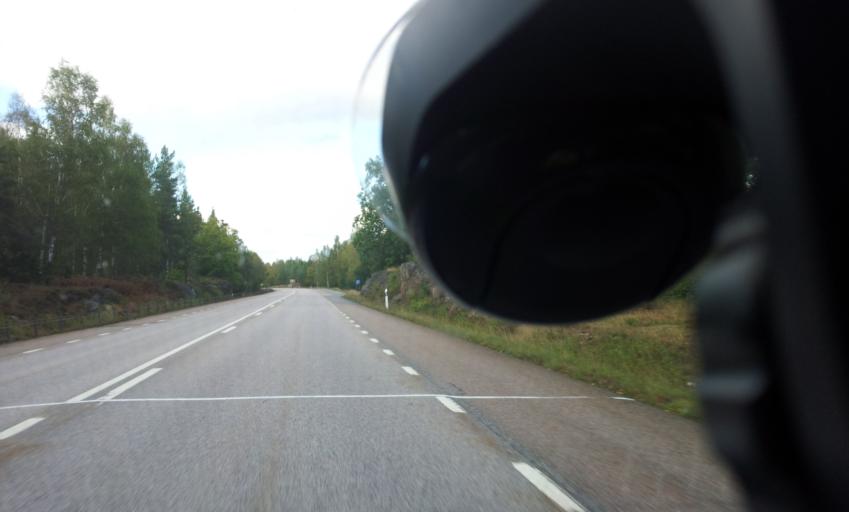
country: SE
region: Kalmar
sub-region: Oskarshamns Kommun
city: Oskarshamn
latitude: 57.5071
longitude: 16.5023
